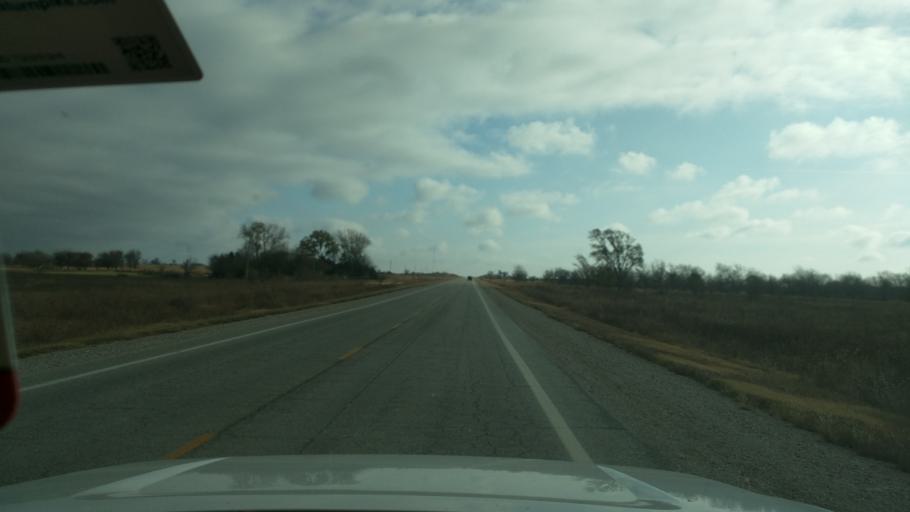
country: US
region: Kansas
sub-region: Chautauqua County
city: Sedan
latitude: 37.0835
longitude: -96.2130
